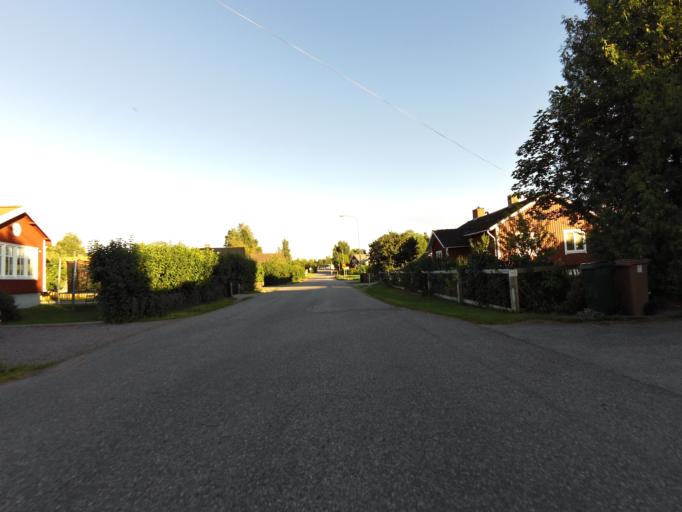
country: SE
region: Gaevleborg
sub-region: Gavle Kommun
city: Gavle
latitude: 60.7175
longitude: 17.1648
